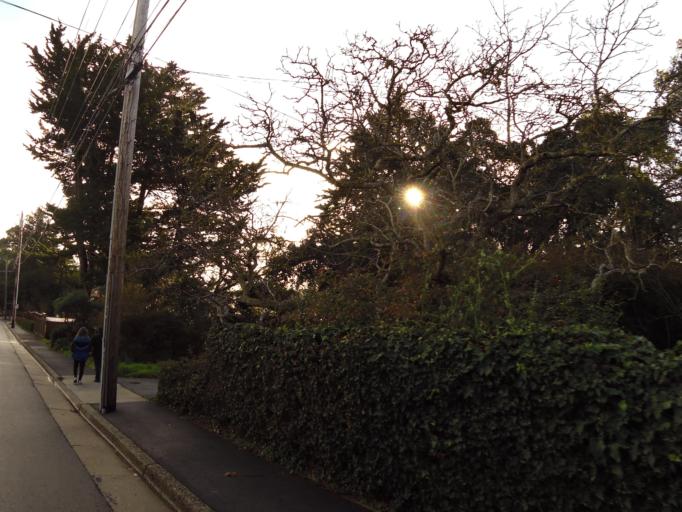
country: US
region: California
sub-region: Santa Cruz County
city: Santa Cruz
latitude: 36.9737
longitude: -122.0584
